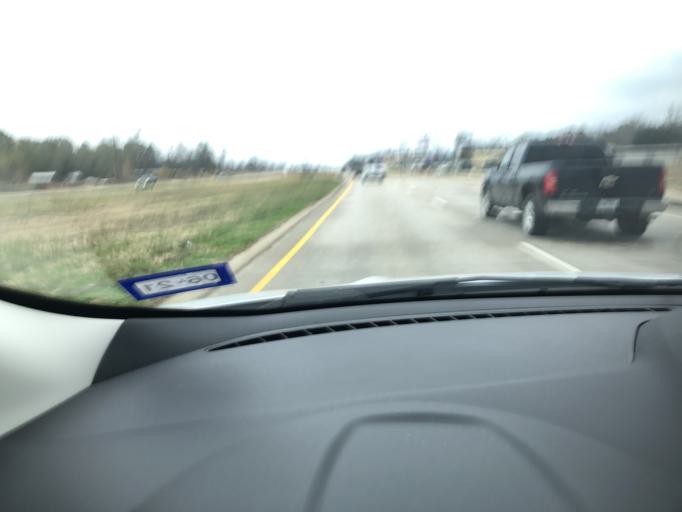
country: US
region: Texas
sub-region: Nacogdoches County
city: Nacogdoches
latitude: 31.5650
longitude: -94.6785
